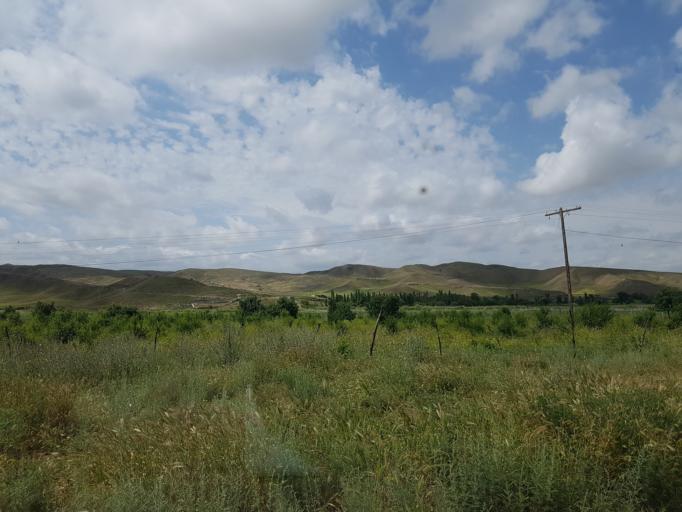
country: TM
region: Ahal
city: Baharly
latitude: 38.2288
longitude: 56.8695
